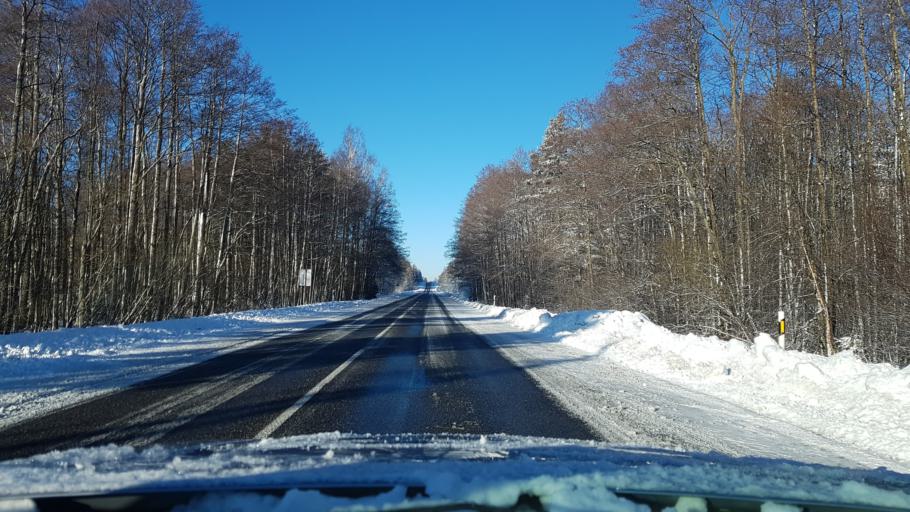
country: EE
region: Hiiumaa
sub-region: Kaerdla linn
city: Kardla
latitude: 58.9564
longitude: 22.8640
